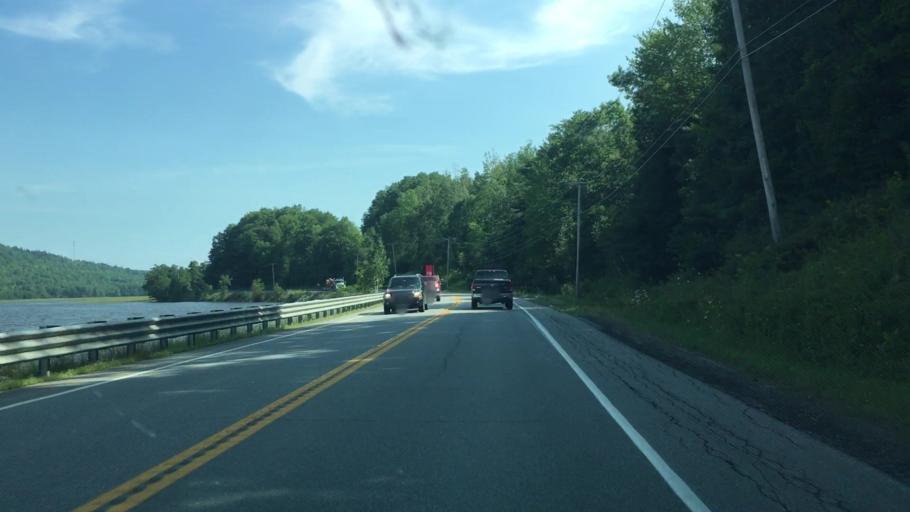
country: US
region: Maine
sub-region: Waldo County
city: Frankfort
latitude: 44.6009
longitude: -68.8679
